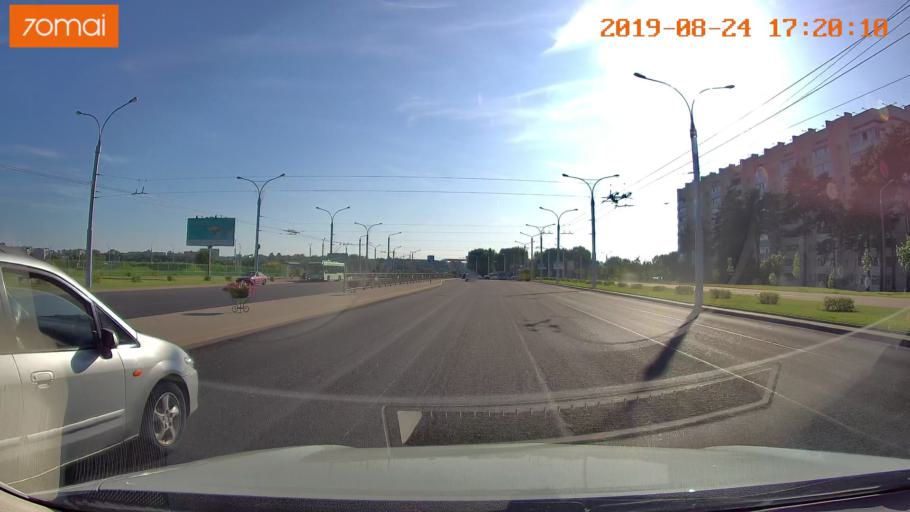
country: BY
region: Minsk
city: Hatava
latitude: 53.8565
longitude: 27.6376
